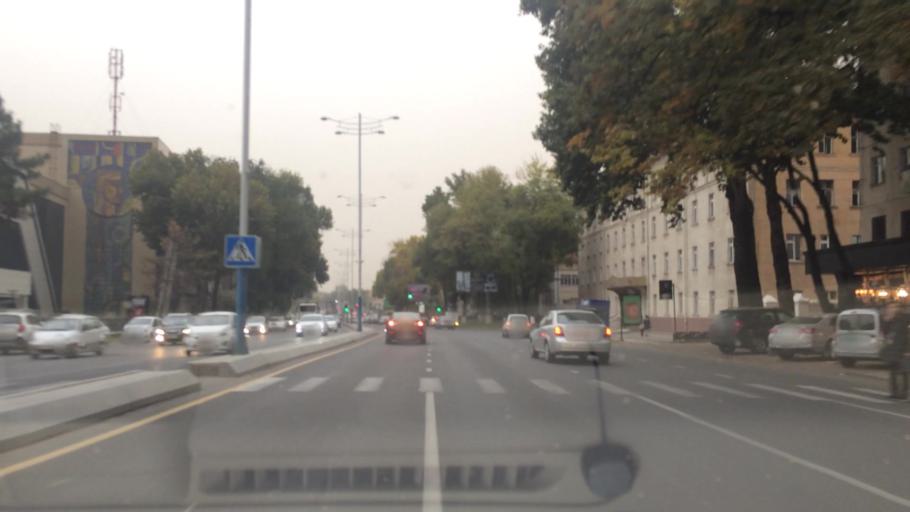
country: UZ
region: Toshkent Shahri
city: Tashkent
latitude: 41.2966
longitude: 69.2503
